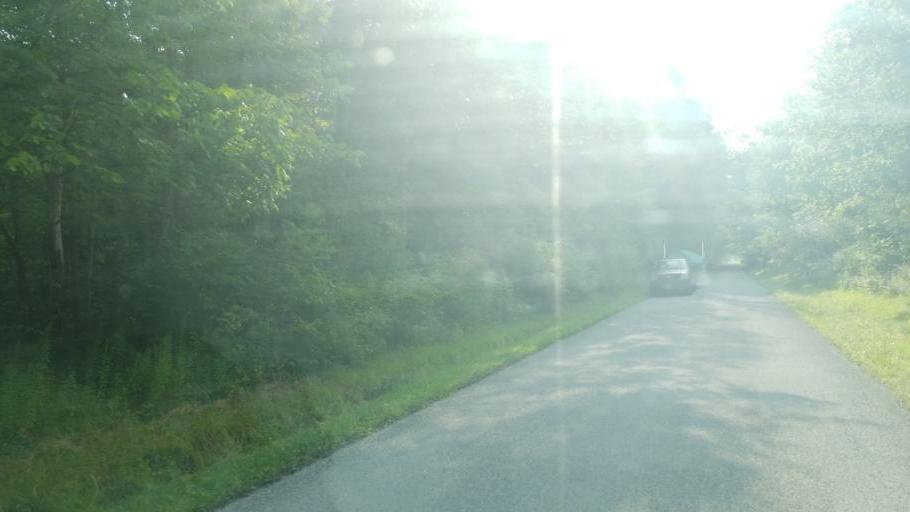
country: US
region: Pennsylvania
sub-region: Crawford County
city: Pymatuning Central
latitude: 41.6256
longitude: -80.4756
